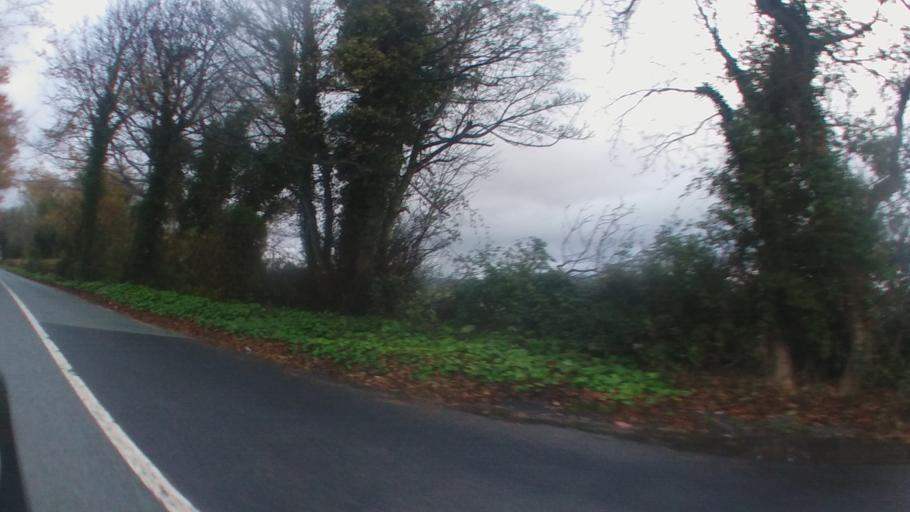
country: IE
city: Kilquade
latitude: 53.0965
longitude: -6.0911
